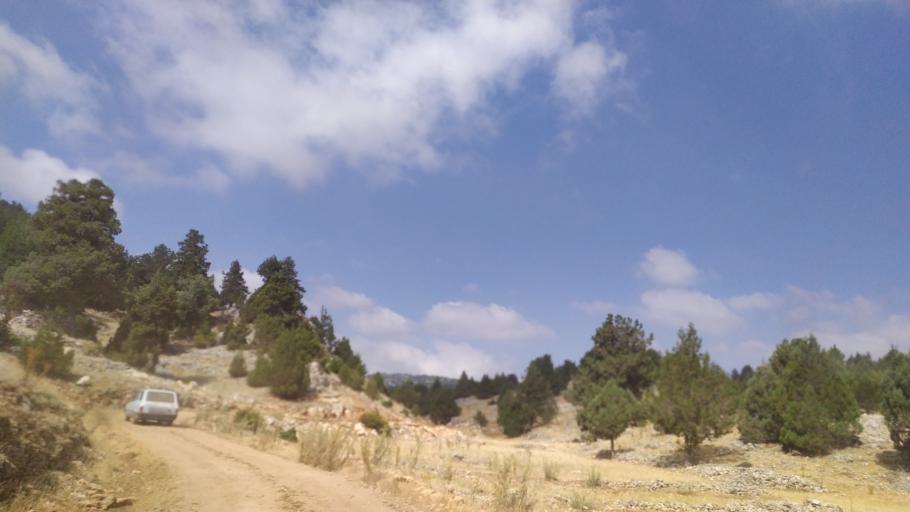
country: TR
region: Mersin
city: Kirobasi
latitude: 36.6169
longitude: 33.8326
